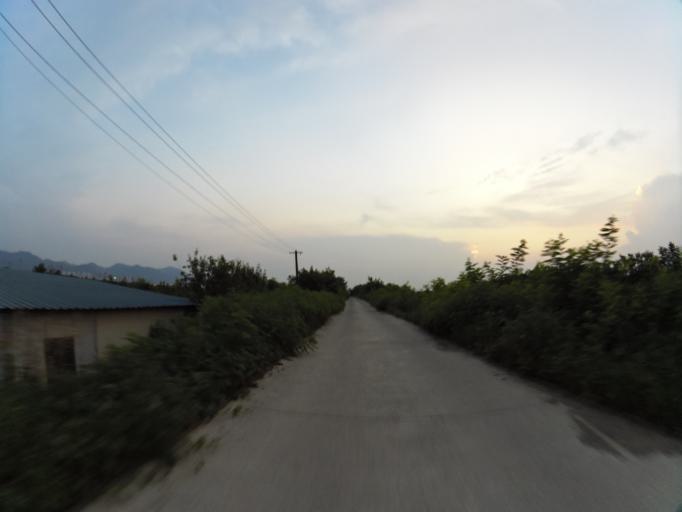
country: KR
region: Gyeongsangbuk-do
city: Gyeongsan-si
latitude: 35.8567
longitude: 128.7491
